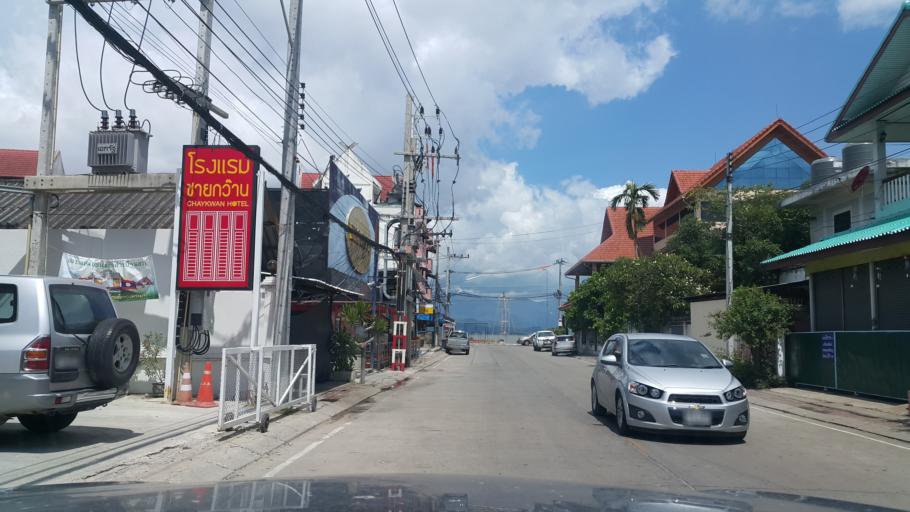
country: TH
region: Phayao
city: Phayao
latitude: 19.1660
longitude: 99.8974
